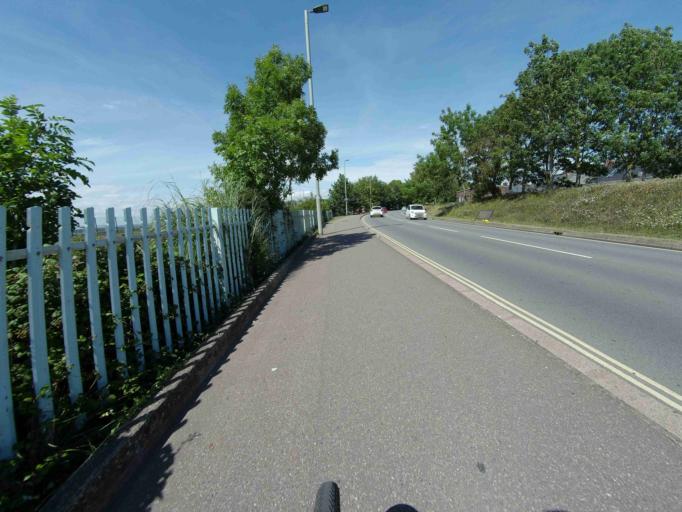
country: GB
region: England
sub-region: Devon
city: Exmouth
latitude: 50.6240
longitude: -3.4152
